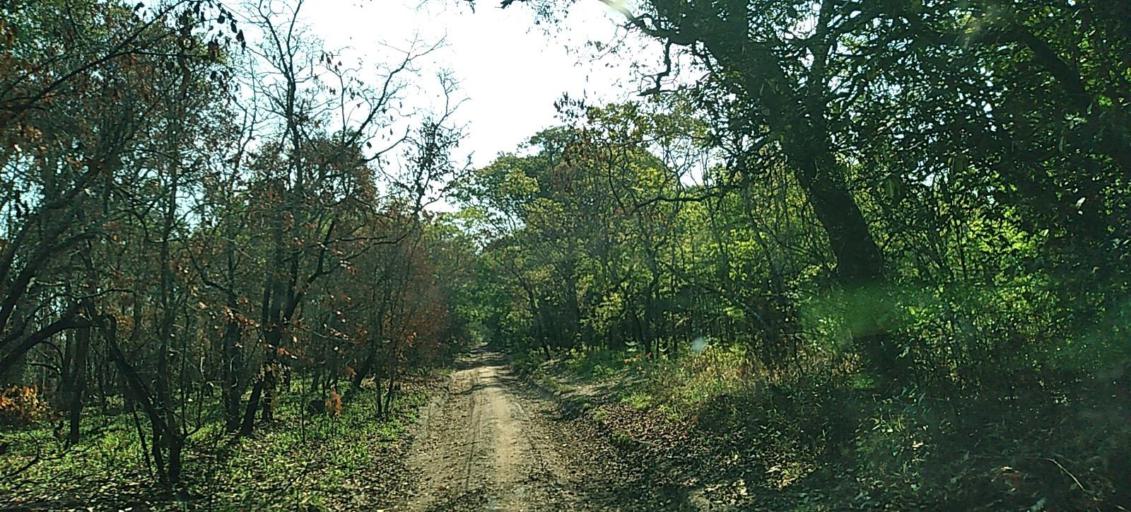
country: ZM
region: North-Western
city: Mwinilunga
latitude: -11.3020
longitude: 24.8411
